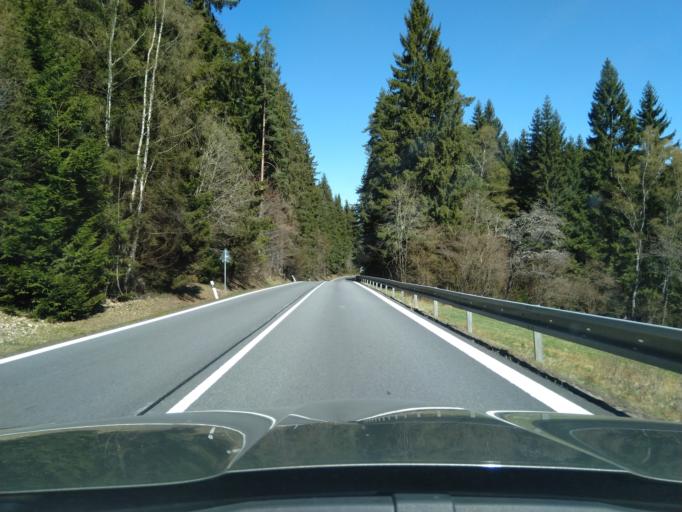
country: CZ
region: Jihocesky
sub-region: Okres Prachatice
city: Vimperk
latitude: 49.0047
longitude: 13.7653
